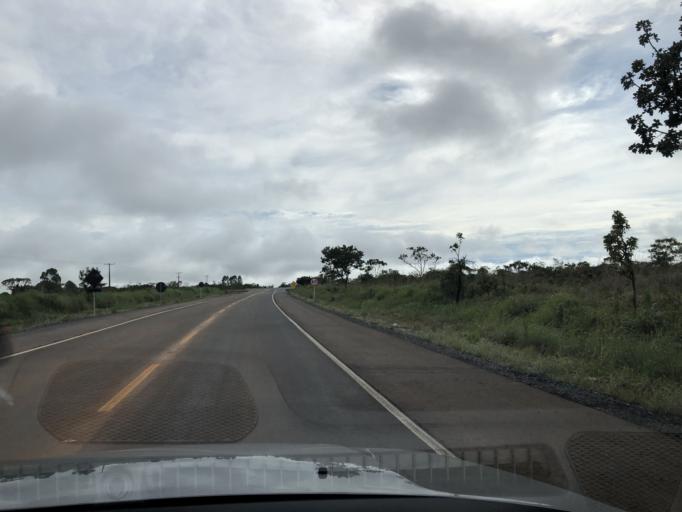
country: BR
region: Federal District
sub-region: Brasilia
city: Brasilia
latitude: -15.6246
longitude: -48.0700
